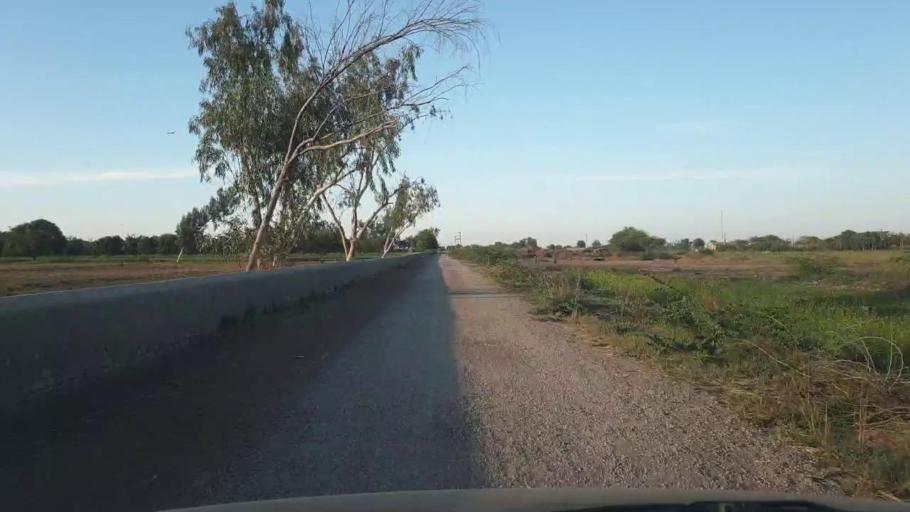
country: PK
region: Sindh
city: Dhoro Naro
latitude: 25.3940
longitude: 69.5755
